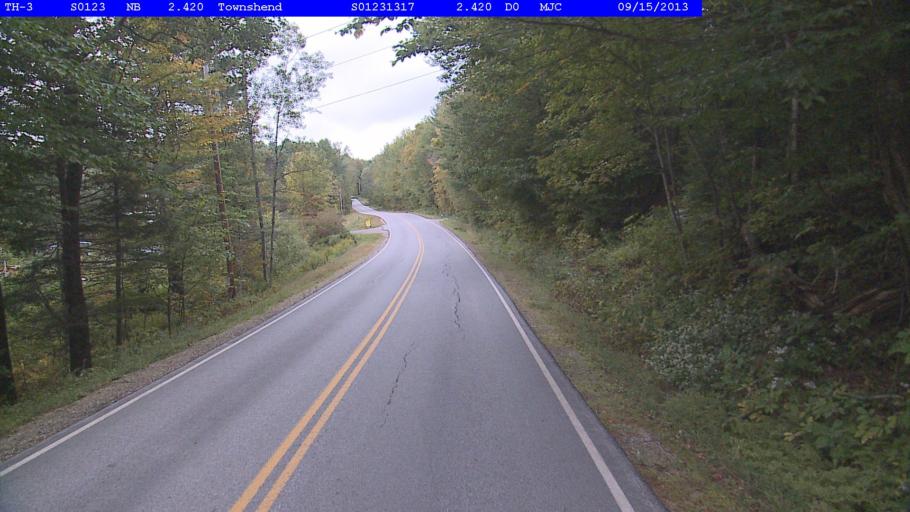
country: US
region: Vermont
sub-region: Windham County
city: Newfane
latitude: 43.1173
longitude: -72.7086
